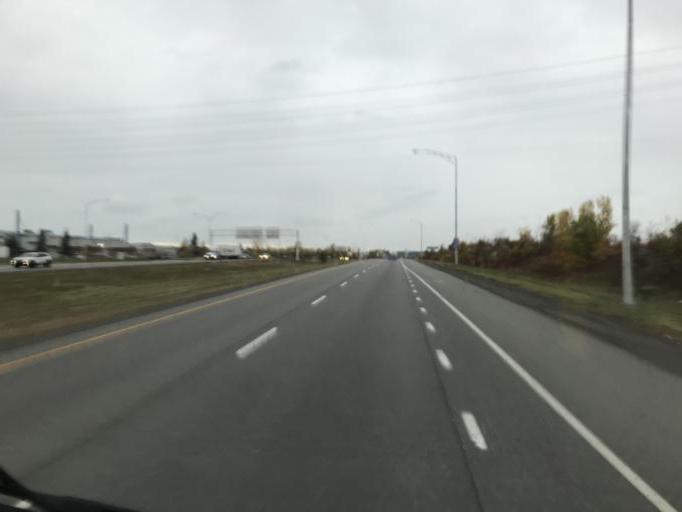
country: CA
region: Quebec
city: Bois-des-Filion
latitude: 45.6809
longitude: -73.7608
